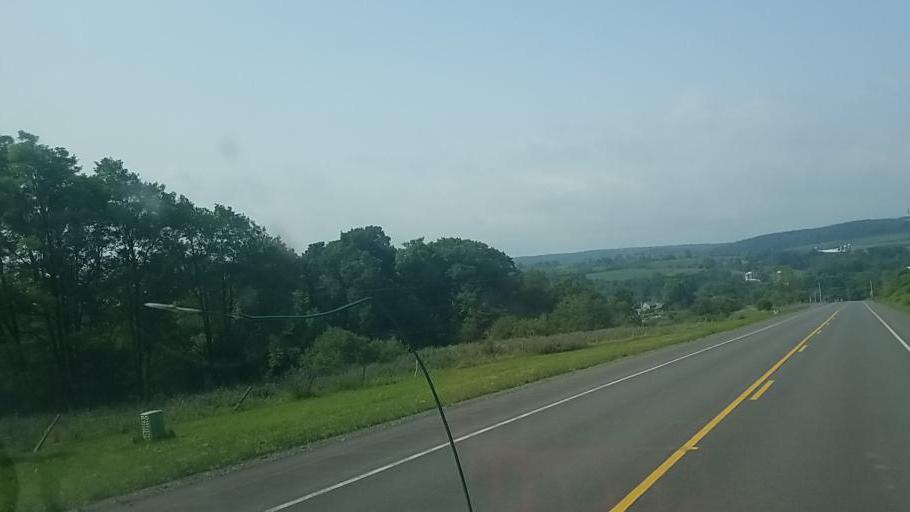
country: US
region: New York
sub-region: Fulton County
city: Johnstown
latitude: 42.9930
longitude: -74.4248
